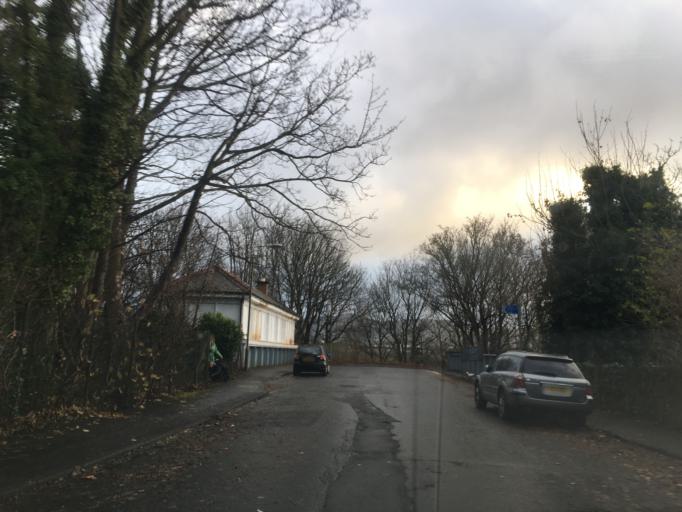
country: GB
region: Scotland
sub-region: Edinburgh
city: Colinton
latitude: 55.9420
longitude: -3.2650
